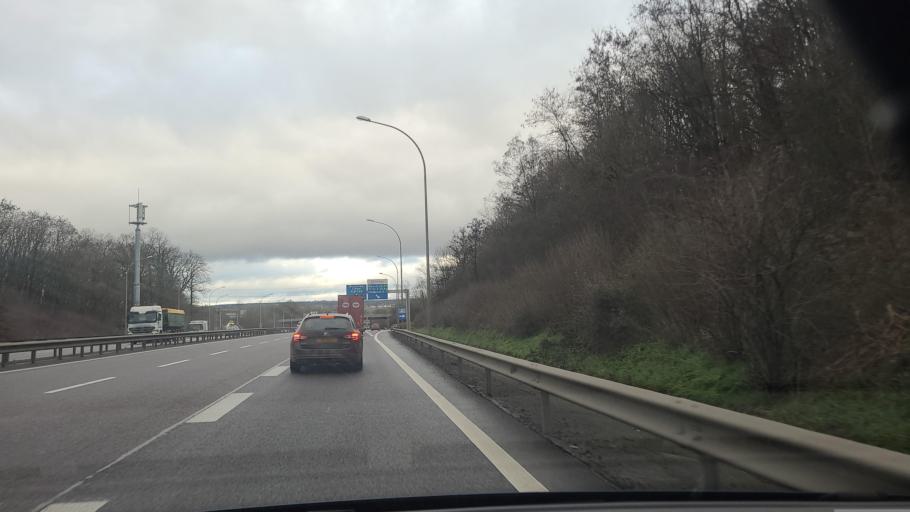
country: LU
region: Luxembourg
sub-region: Canton d'Esch-sur-Alzette
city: Leudelange
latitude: 49.5811
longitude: 6.0878
